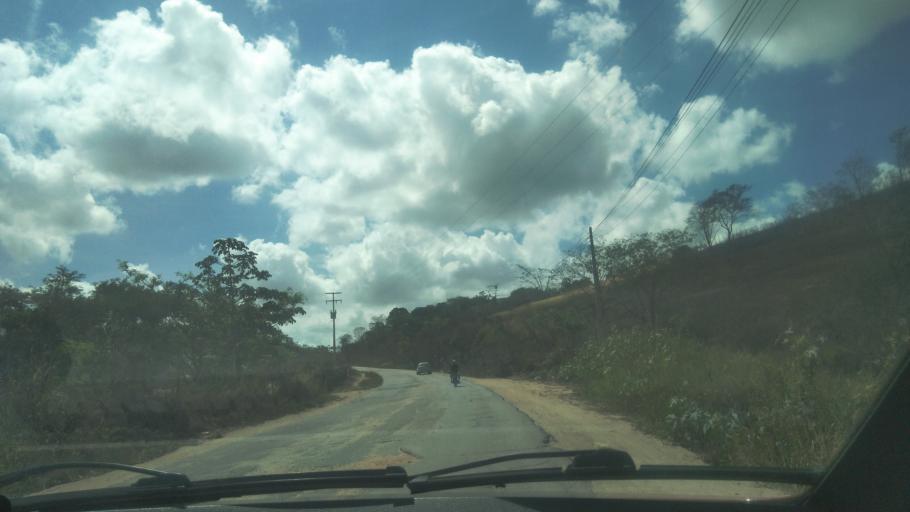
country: BR
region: Pernambuco
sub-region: Vitoria De Santo Antao
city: Vitoria de Santo Antao
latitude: -8.1330
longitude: -35.2808
